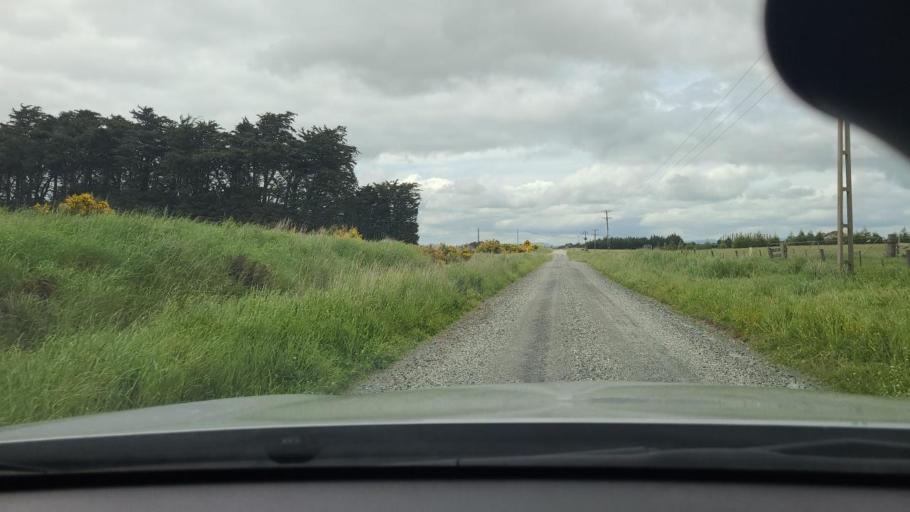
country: NZ
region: Southland
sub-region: Invercargill City
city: Invercargill
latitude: -46.3347
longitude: 168.6788
